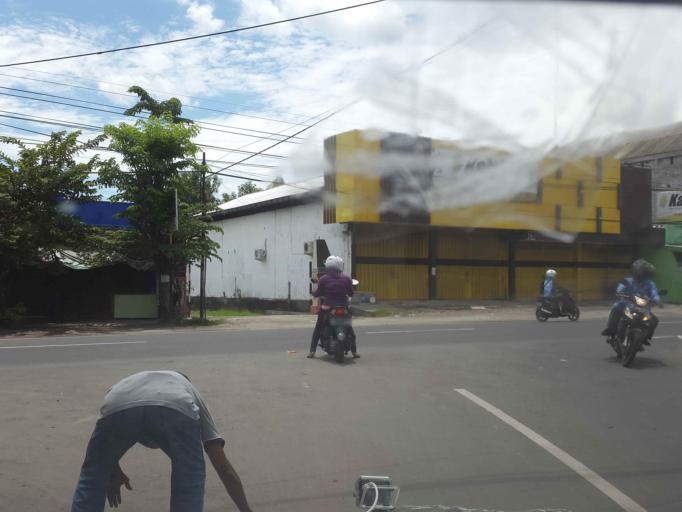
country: ID
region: East Java
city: Madiun
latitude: -7.5904
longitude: 111.5386
